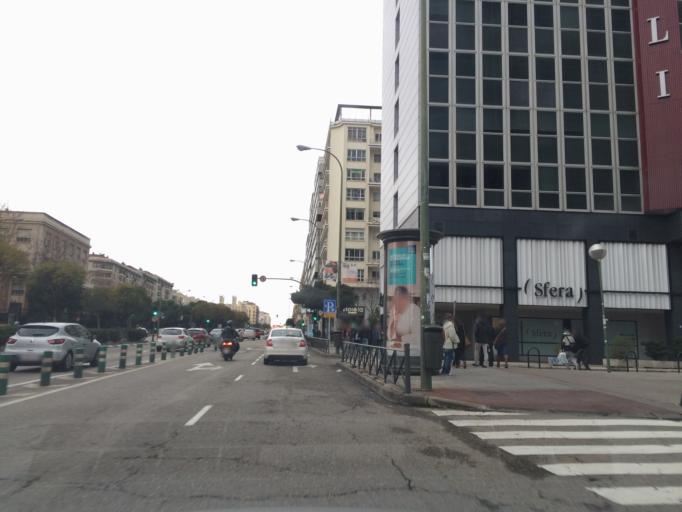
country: ES
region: Madrid
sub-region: Provincia de Madrid
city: Chamberi
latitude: 40.4465
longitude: -3.6947
